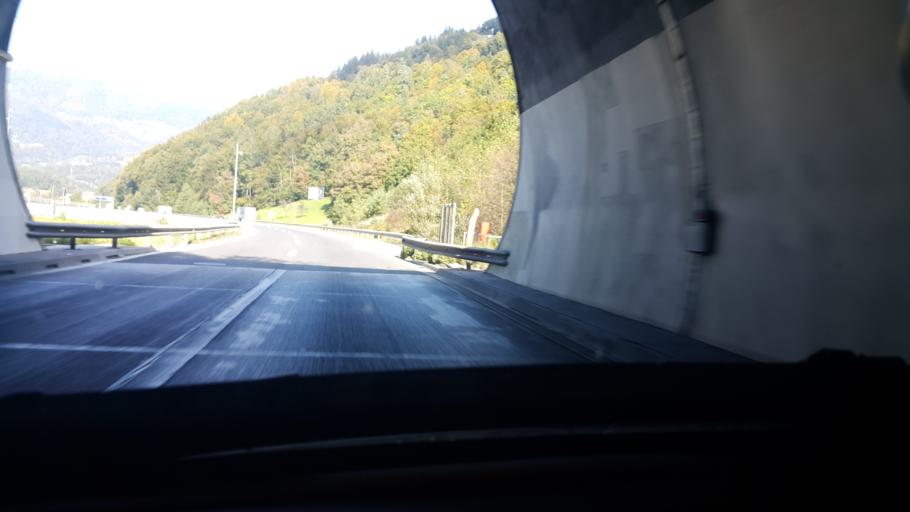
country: SI
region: Vransko
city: Vransko
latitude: 46.2228
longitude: 14.9463
